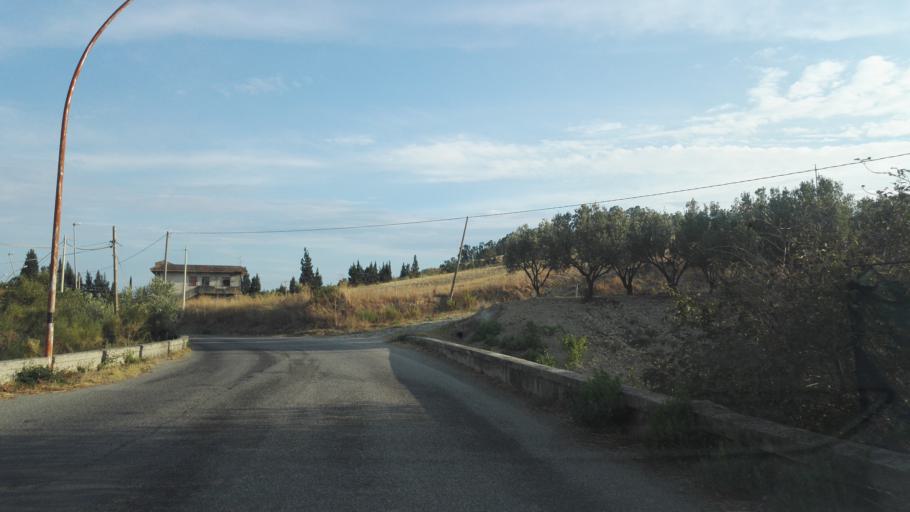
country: IT
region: Calabria
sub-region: Provincia di Reggio Calabria
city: Caulonia Marina
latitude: 38.3756
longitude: 16.4820
